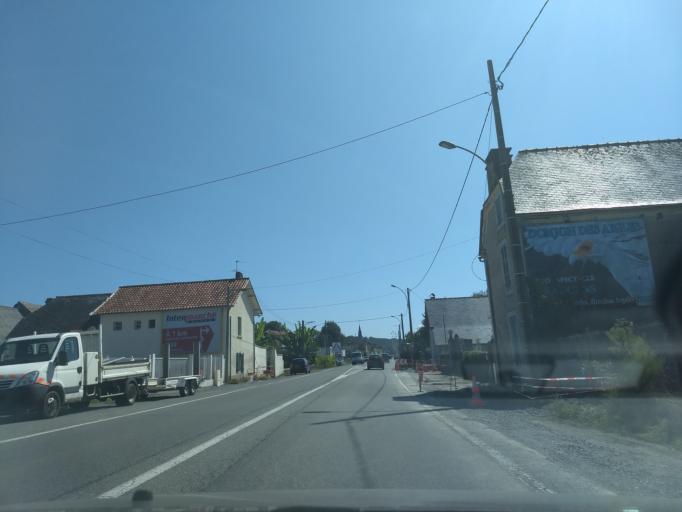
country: FR
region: Aquitaine
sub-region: Departement des Pyrenees-Atlantiques
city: Soumoulou
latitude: 43.2693
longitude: -0.1982
